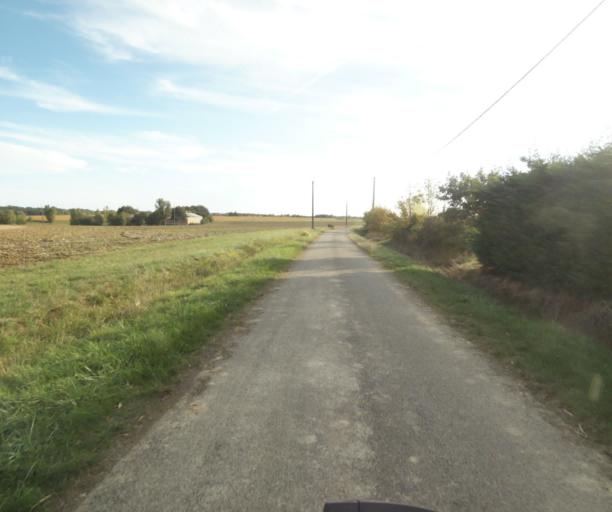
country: FR
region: Midi-Pyrenees
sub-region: Departement du Tarn-et-Garonne
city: Finhan
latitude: 43.9129
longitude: 1.1311
